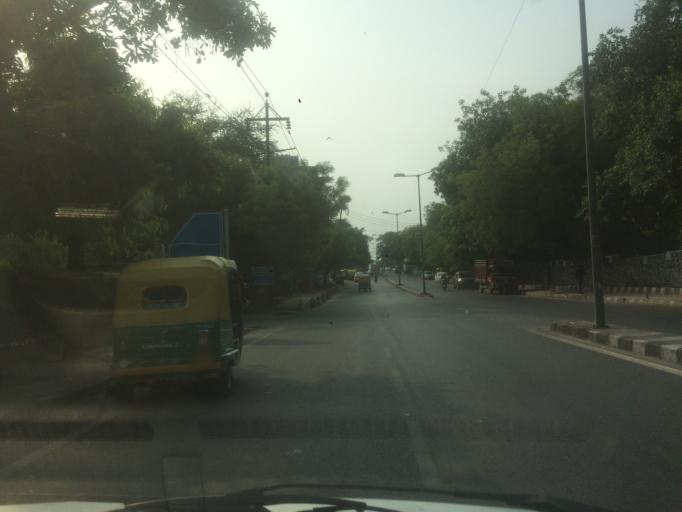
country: IN
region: NCT
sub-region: New Delhi
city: New Delhi
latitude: 28.5526
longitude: 77.1679
